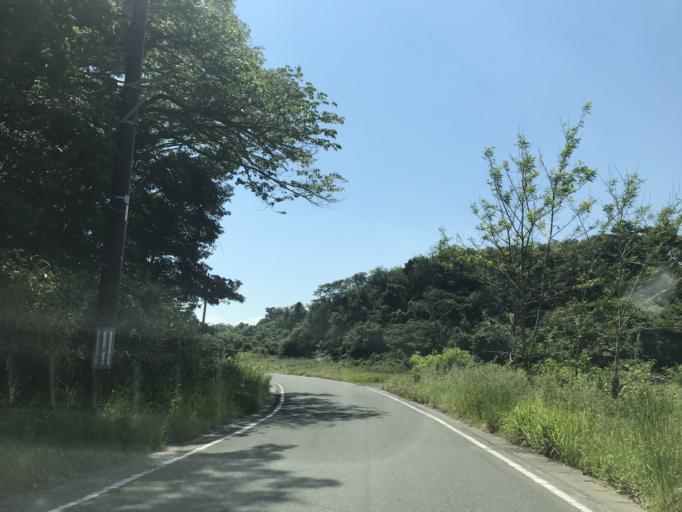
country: JP
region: Miyagi
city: Matsushima
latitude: 38.3284
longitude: 141.1613
